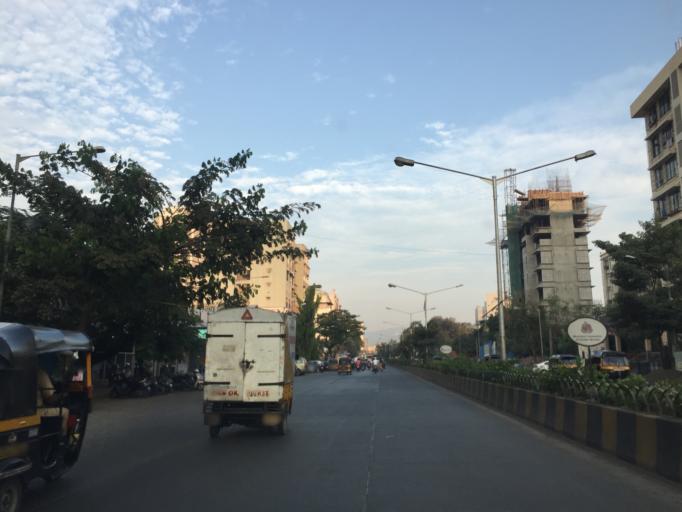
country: IN
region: Maharashtra
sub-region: Mumbai Suburban
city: Borivli
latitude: 19.2204
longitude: 72.8488
